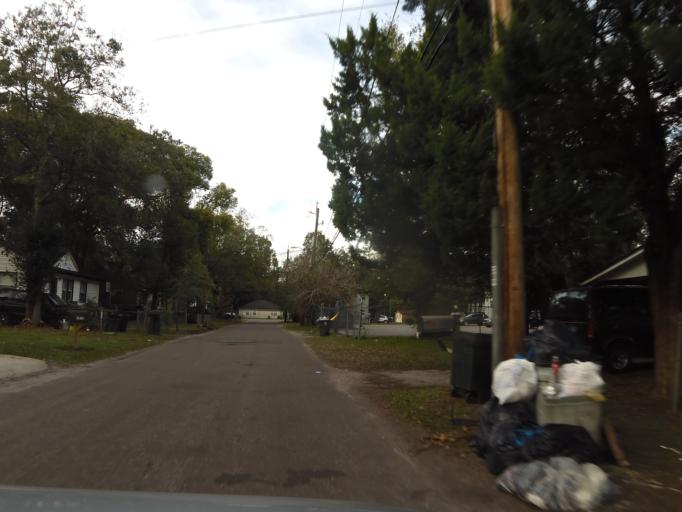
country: US
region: Florida
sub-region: Duval County
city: Jacksonville
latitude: 30.3391
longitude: -81.7163
